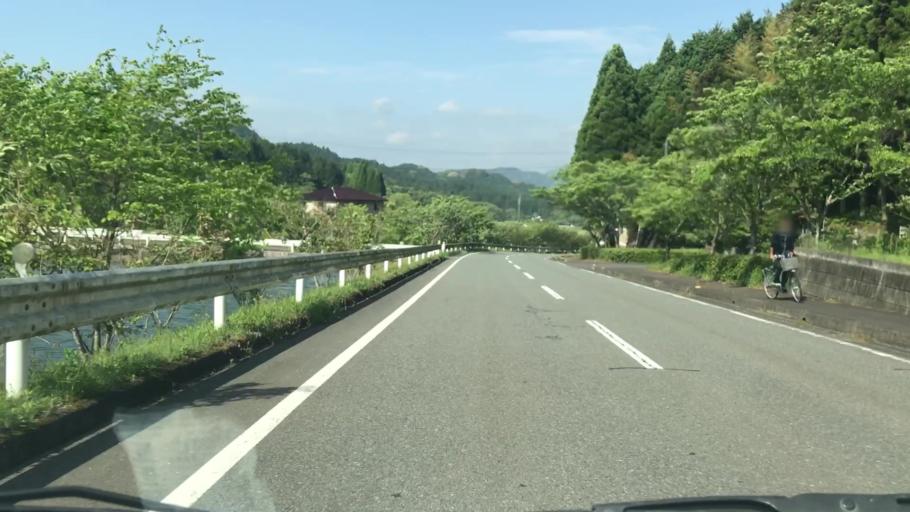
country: JP
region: Saga Prefecture
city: Takeocho-takeo
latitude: 33.2154
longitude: 129.9975
